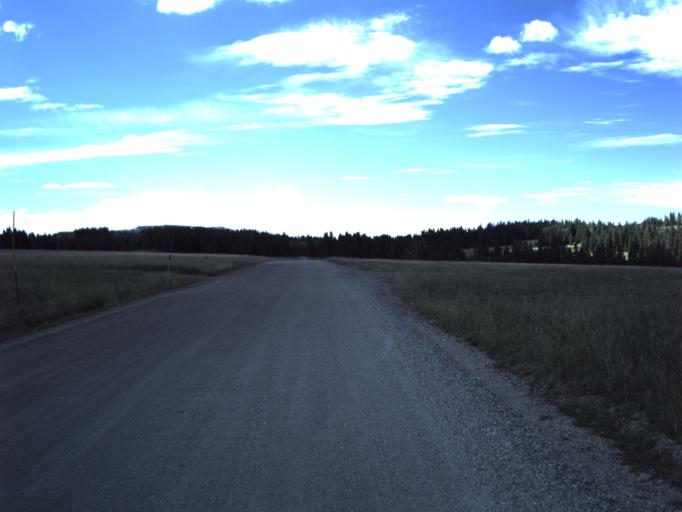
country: US
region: Utah
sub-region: Piute County
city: Junction
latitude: 38.2748
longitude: -112.3650
